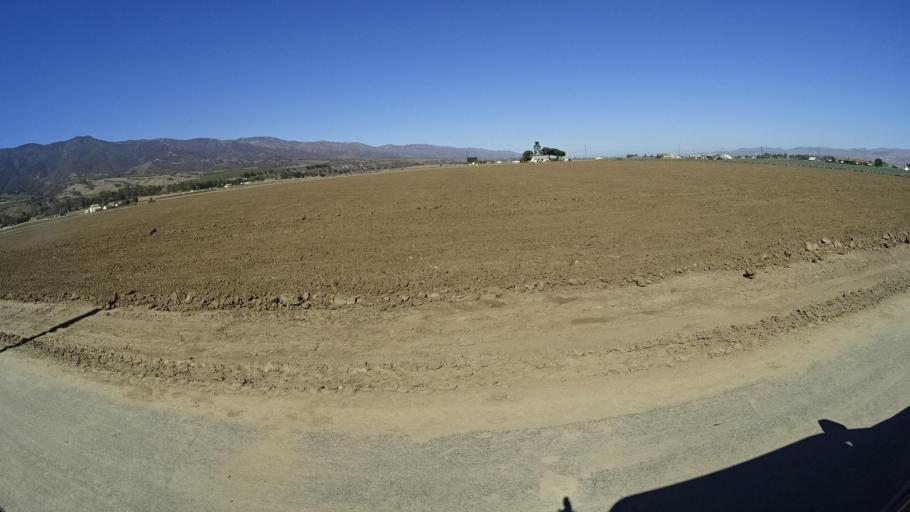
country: US
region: California
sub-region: Monterey County
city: Soledad
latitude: 36.3931
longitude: -121.3496
